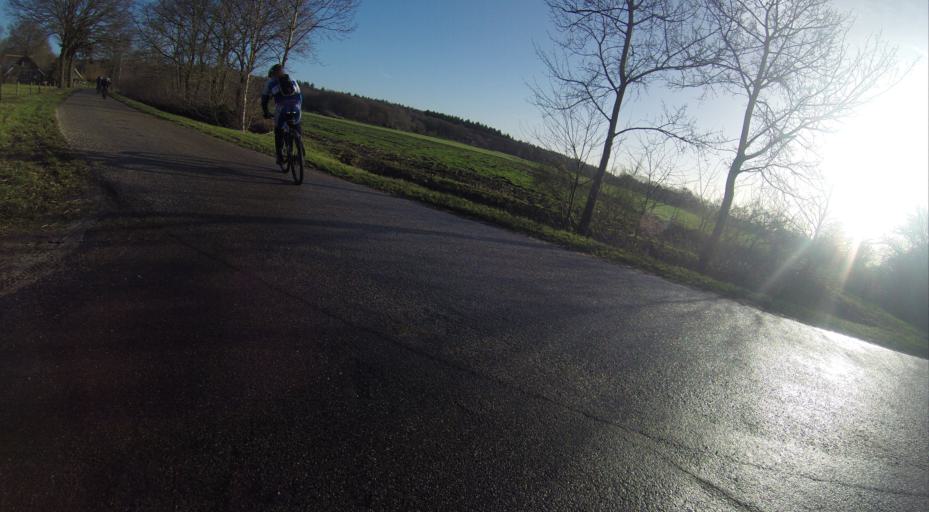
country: NL
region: Gelderland
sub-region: Gemeente Lochem
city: Laren
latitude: 52.2979
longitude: 6.3976
